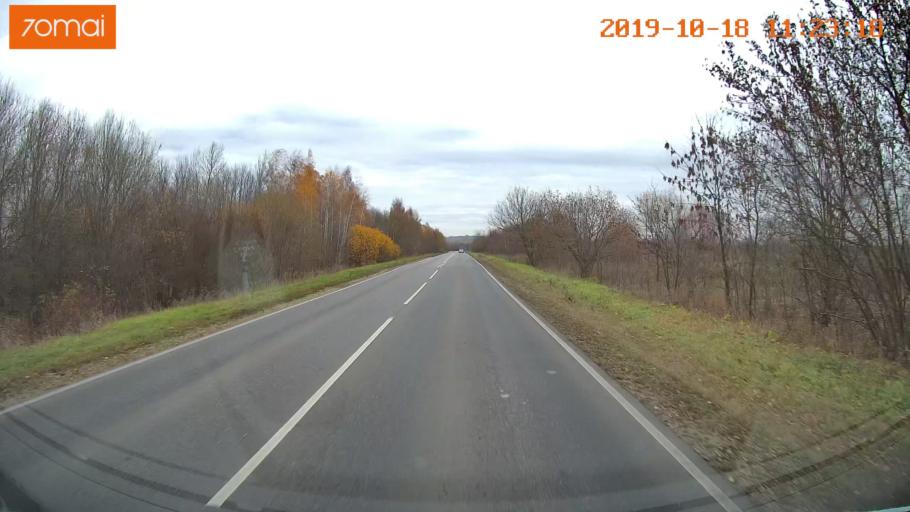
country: RU
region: Tula
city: Kimovsk
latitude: 54.0997
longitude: 38.5925
